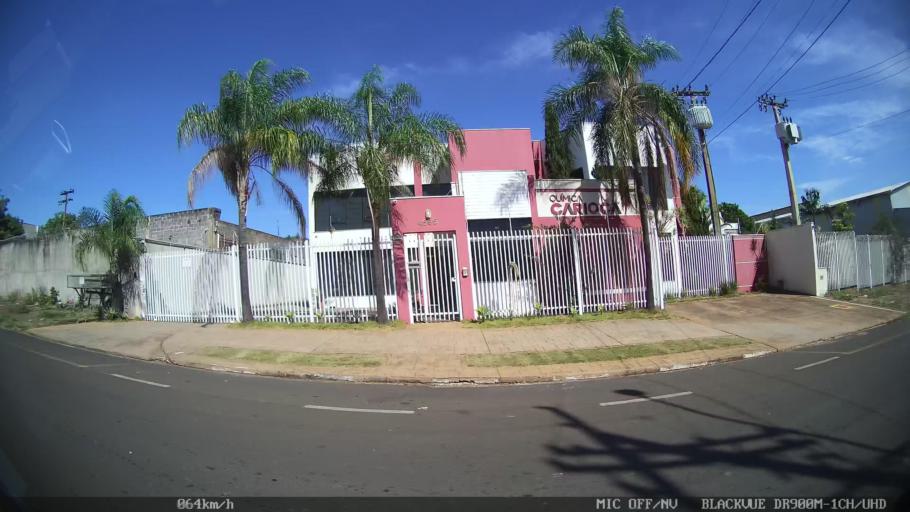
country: BR
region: Sao Paulo
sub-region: Franca
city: Franca
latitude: -20.5470
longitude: -47.4560
